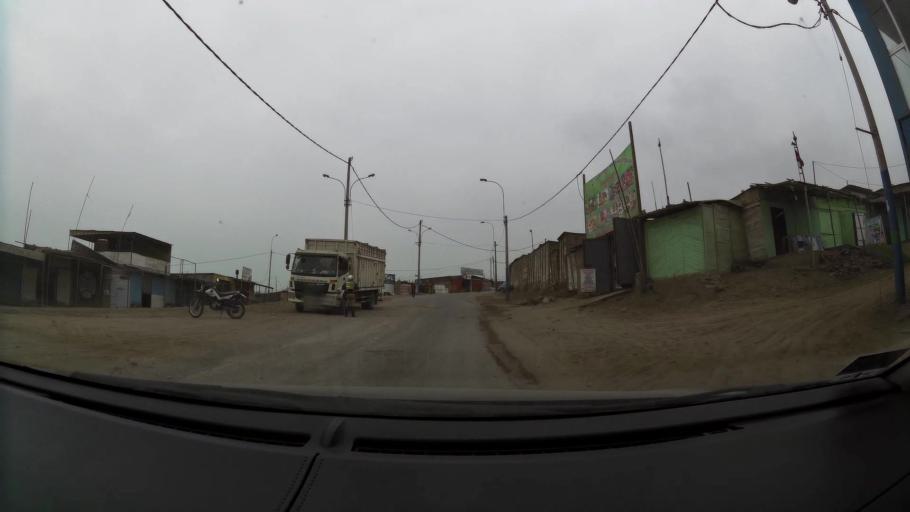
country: PE
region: Lima
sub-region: Lima
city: Santa Rosa
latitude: -11.8395
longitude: -77.1556
